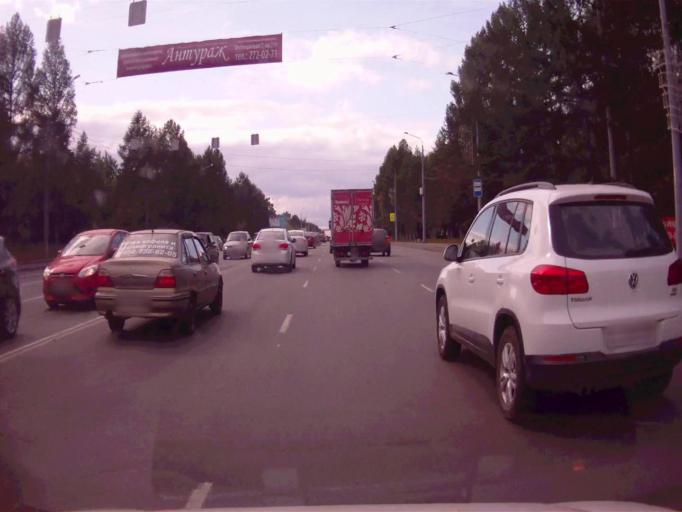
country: RU
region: Chelyabinsk
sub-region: Gorod Chelyabinsk
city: Chelyabinsk
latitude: 55.1474
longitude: 61.3643
